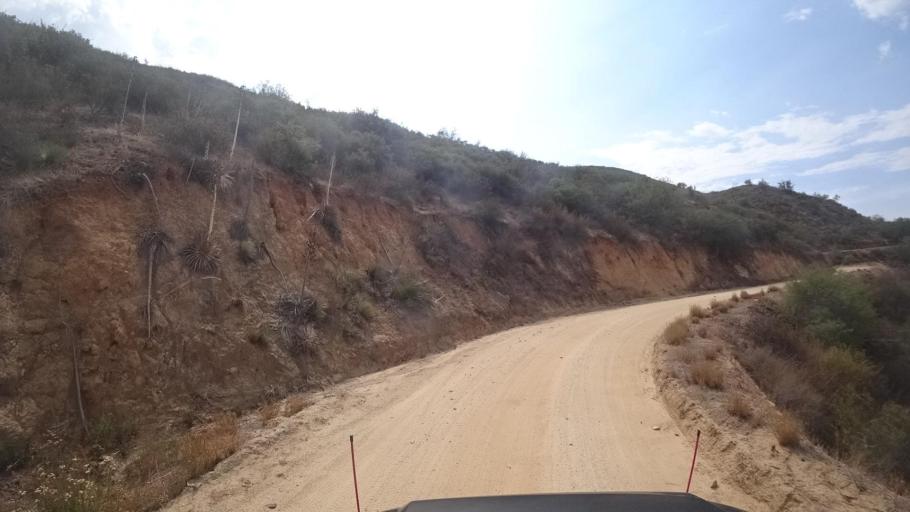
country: US
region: California
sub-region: San Diego County
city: Ramona
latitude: 33.1147
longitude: -116.8169
